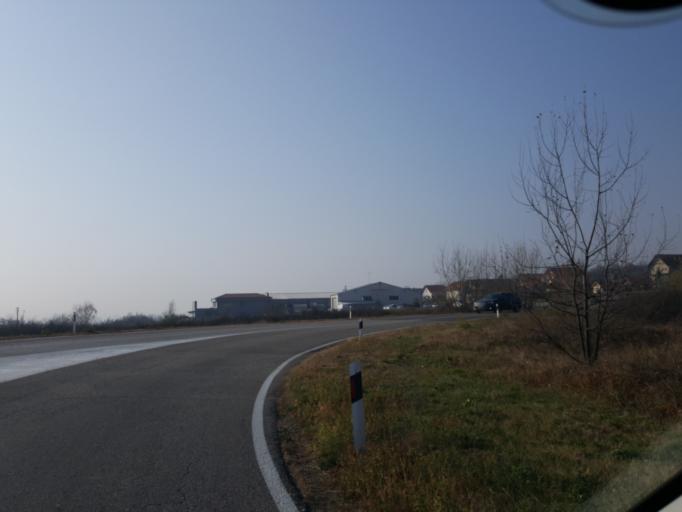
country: RS
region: Central Serbia
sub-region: Zajecarski Okrug
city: Zajecar
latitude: 43.9229
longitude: 22.2961
